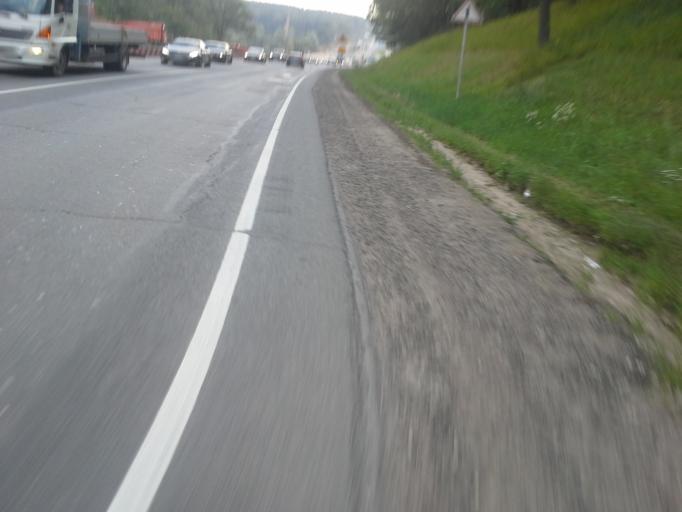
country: RU
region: Moskovskaya
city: Snegiri
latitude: 55.8621
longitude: 36.9390
